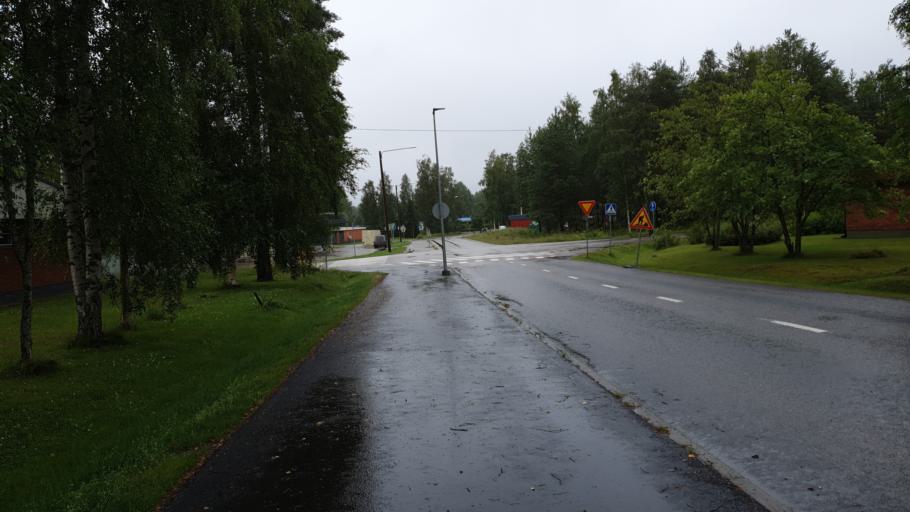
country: FI
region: Kainuu
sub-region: Kehys-Kainuu
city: Kuhmo
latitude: 64.1208
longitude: 29.5285
